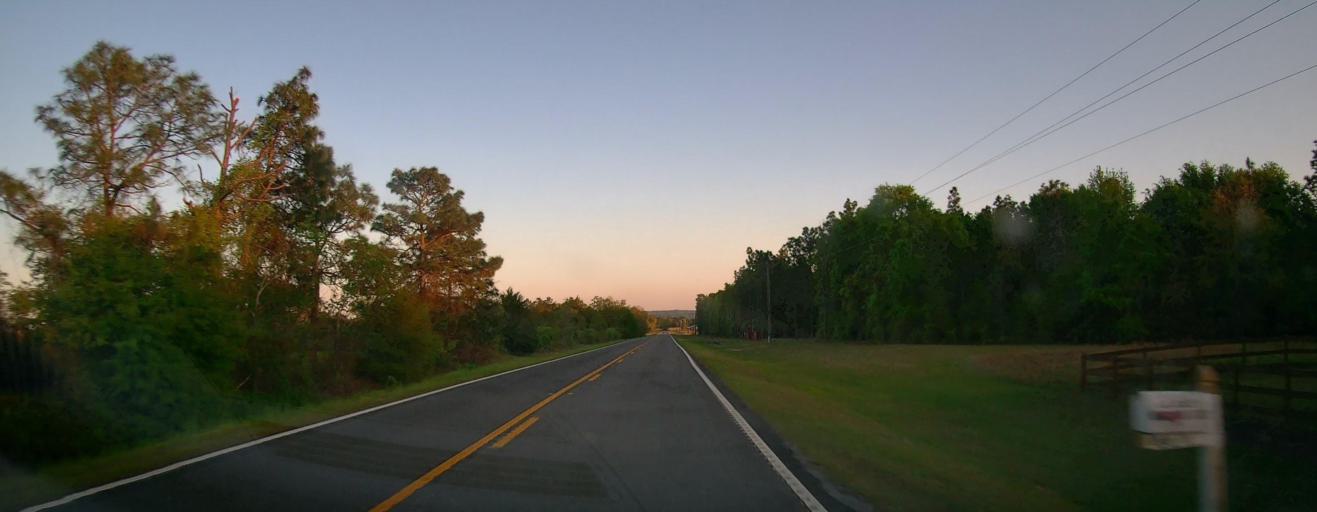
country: US
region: Georgia
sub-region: Marion County
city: Buena Vista
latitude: 32.4656
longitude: -84.6333
